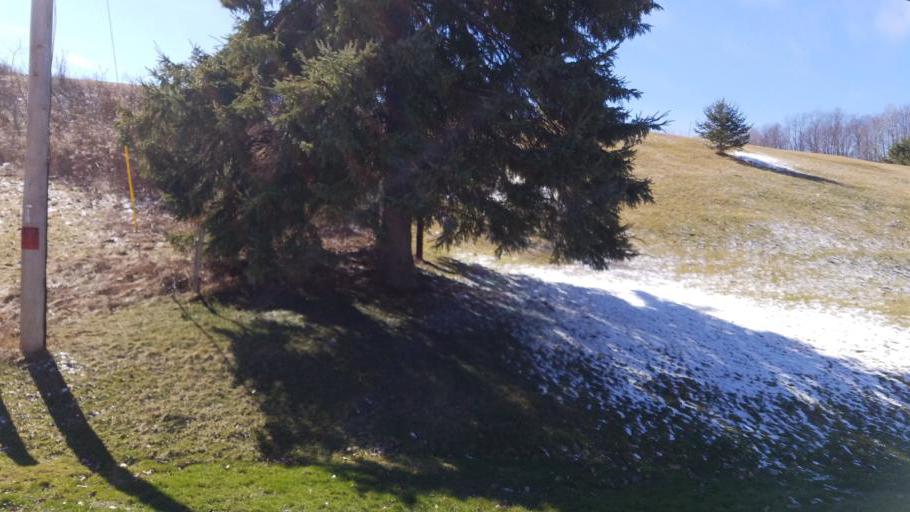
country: US
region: New York
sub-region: Allegany County
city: Wellsville
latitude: 42.0764
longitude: -77.9320
